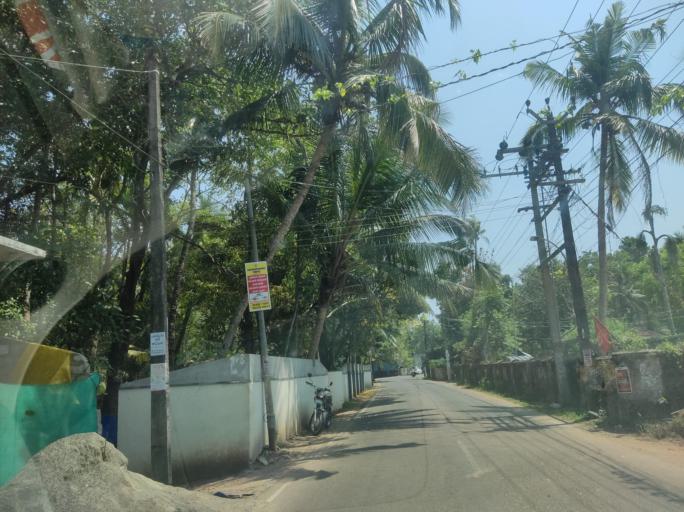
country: IN
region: Kerala
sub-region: Alappuzha
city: Kutiatodu
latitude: 9.8387
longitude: 76.2963
